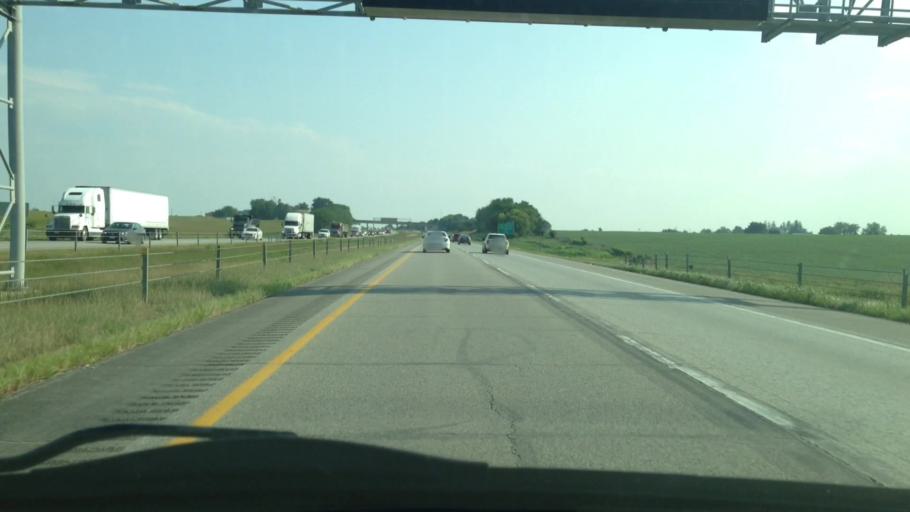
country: US
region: Iowa
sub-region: Linn County
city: Ely
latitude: 41.9129
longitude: -91.6716
